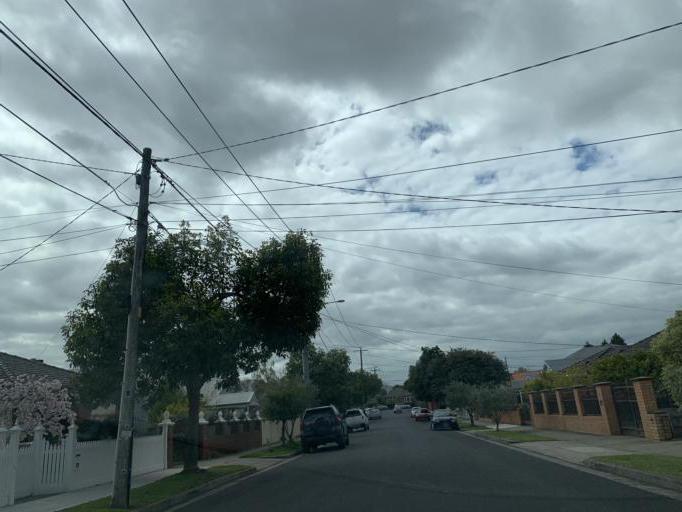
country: AU
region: Victoria
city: Thornbury
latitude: -37.7364
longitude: 144.9930
